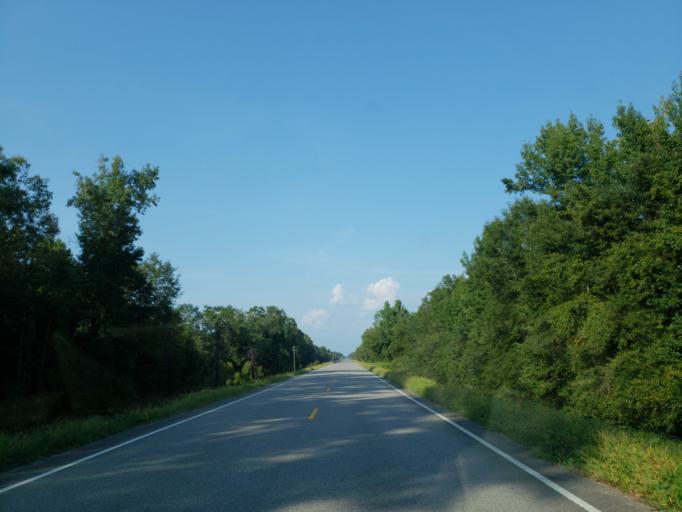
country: US
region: Alabama
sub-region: Sumter County
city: Livingston
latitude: 32.7102
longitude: -88.0811
